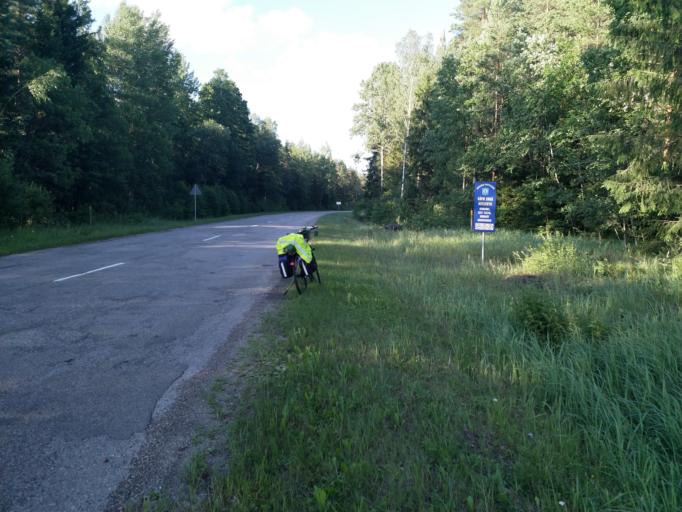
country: LV
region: Rojas
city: Roja
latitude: 57.4785
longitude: 22.7041
